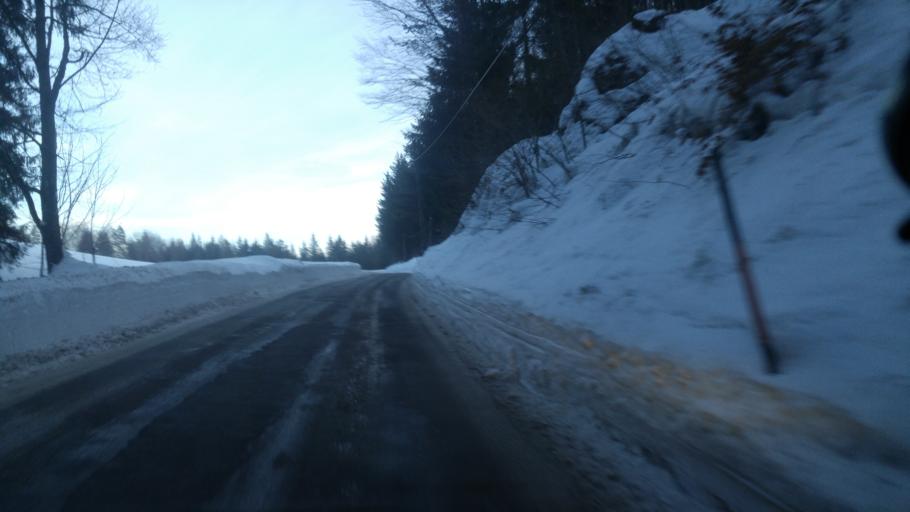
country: AT
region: Lower Austria
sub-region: Politischer Bezirk Lilienfeld
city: Hohenberg
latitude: 47.8920
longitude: 15.6742
